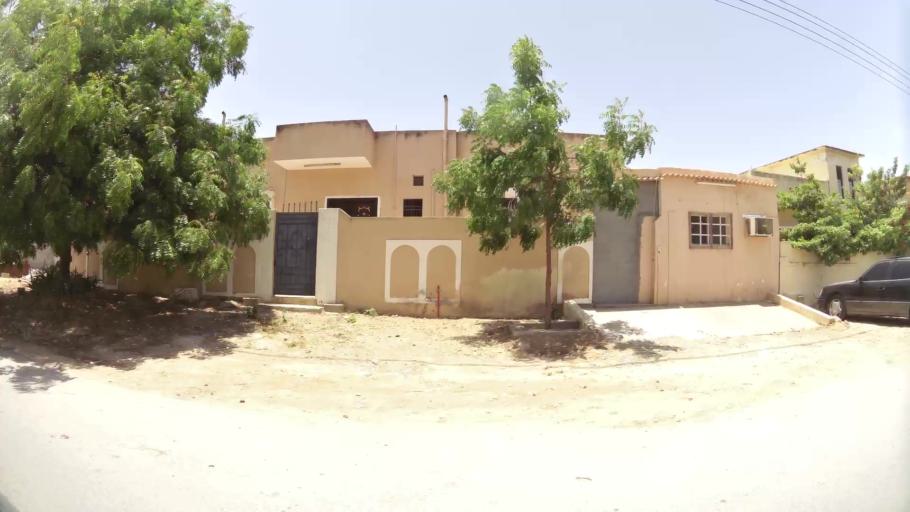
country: OM
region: Zufar
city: Salalah
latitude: 17.0718
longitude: 54.1552
